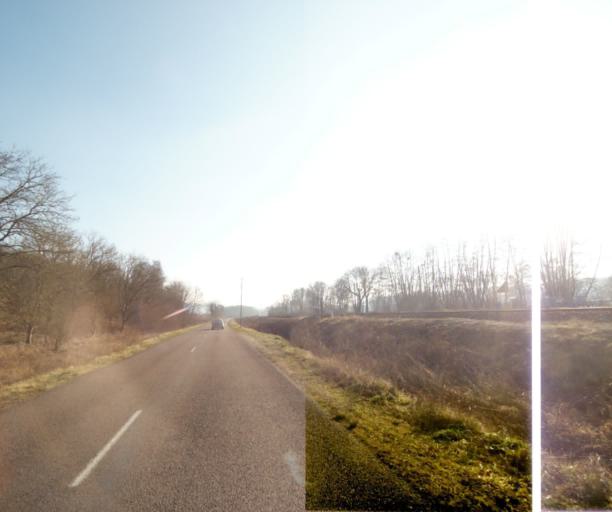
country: FR
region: Champagne-Ardenne
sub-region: Departement de la Haute-Marne
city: Chevillon
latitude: 48.5068
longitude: 5.1244
